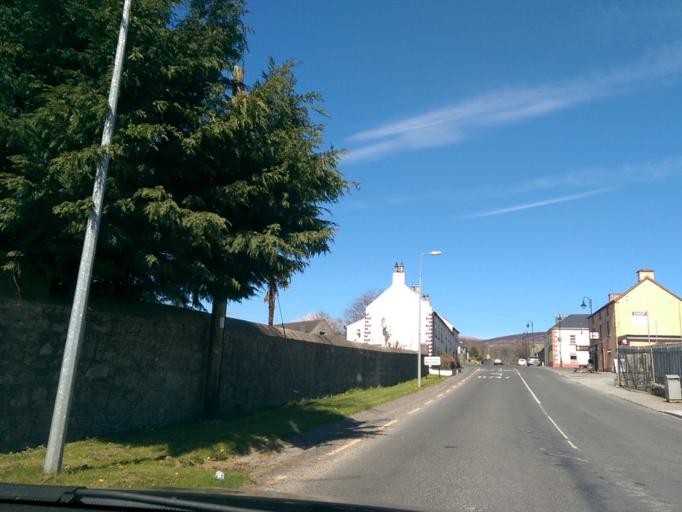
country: IE
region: Leinster
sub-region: Wicklow
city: Baltinglass
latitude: 52.9036
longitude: -6.6073
